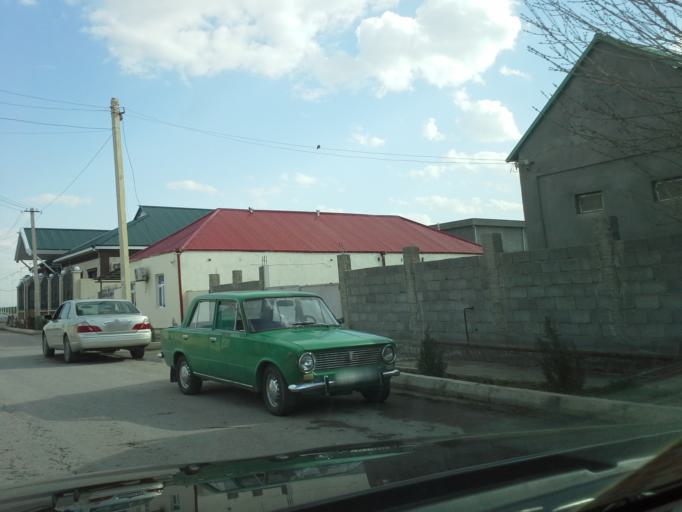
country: TM
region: Ahal
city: Ashgabat
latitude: 37.9930
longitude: 58.2988
